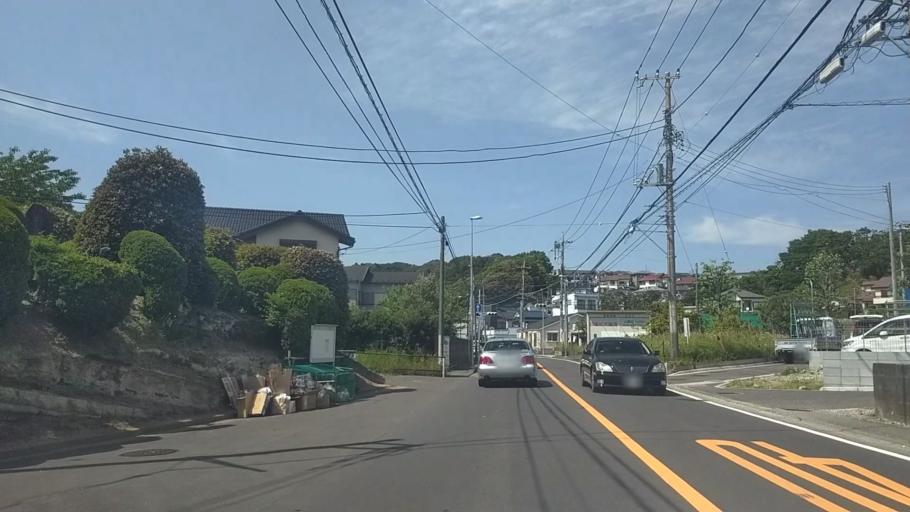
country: JP
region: Kanagawa
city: Kamakura
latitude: 35.3558
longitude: 139.5800
